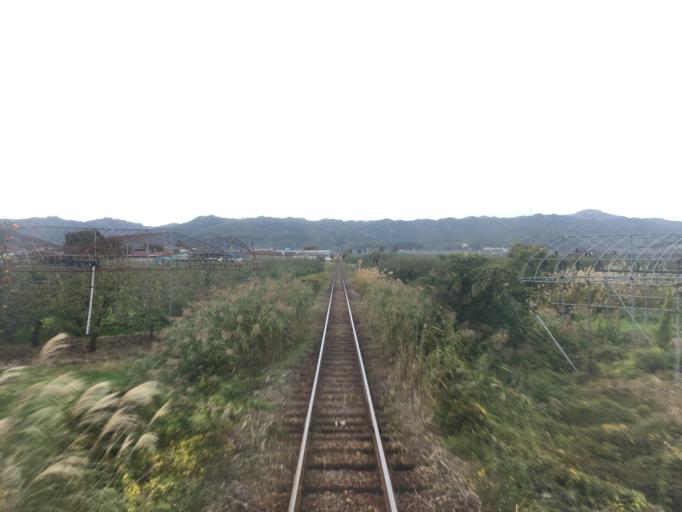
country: JP
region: Yamagata
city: Takahata
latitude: 38.0584
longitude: 140.1470
